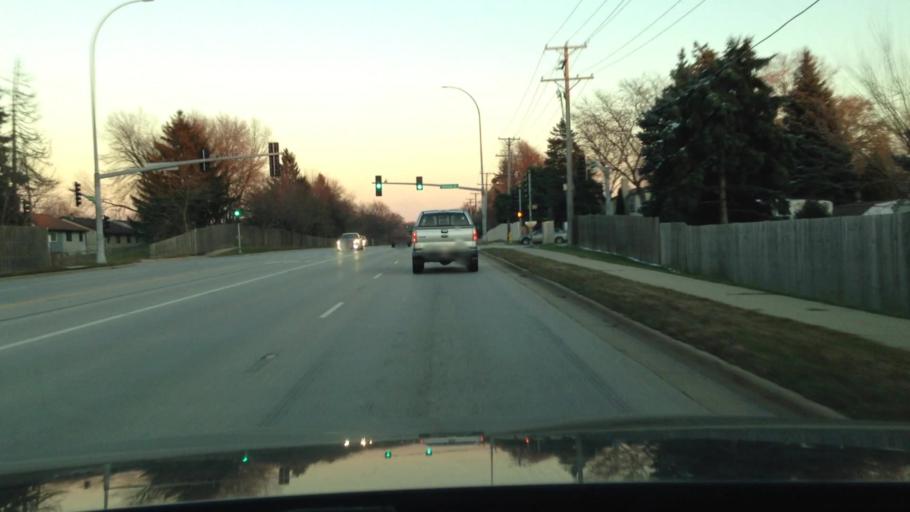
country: US
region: Illinois
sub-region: DuPage County
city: Carol Stream
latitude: 41.9413
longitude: -88.1610
